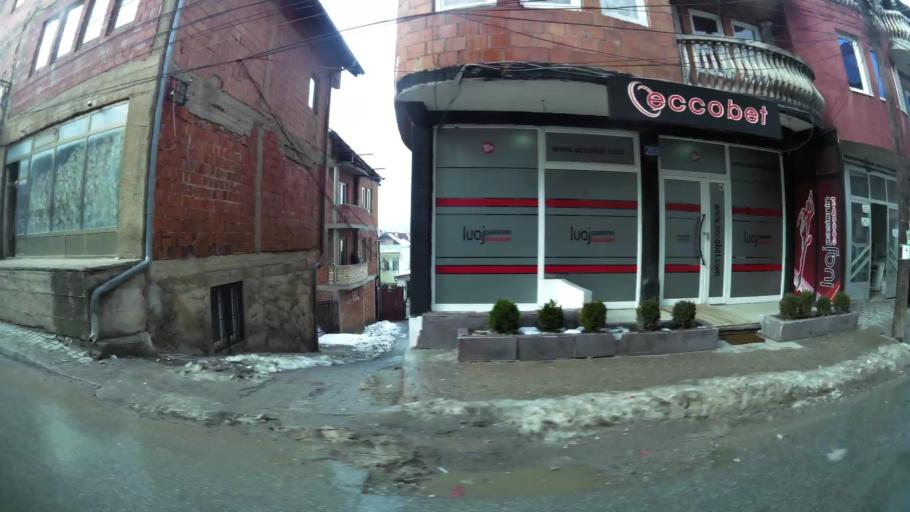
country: XK
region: Pristina
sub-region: Komuna e Prishtines
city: Pristina
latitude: 42.6725
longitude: 21.1725
